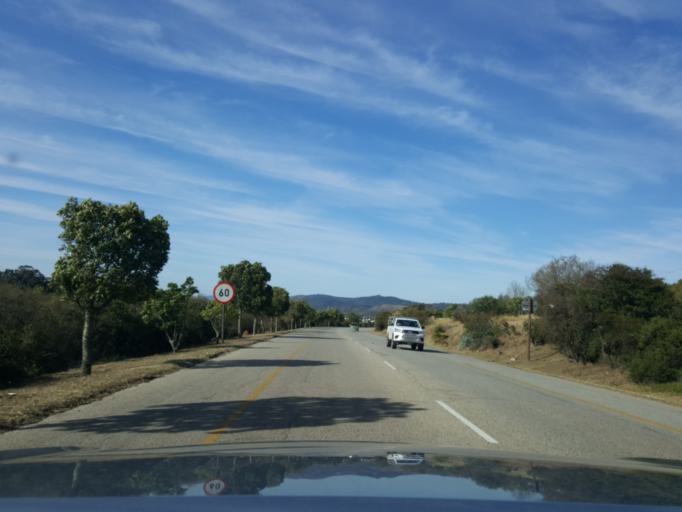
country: ZA
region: Eastern Cape
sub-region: Cacadu District Municipality
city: Grahamstown
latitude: -33.3029
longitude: 26.5047
